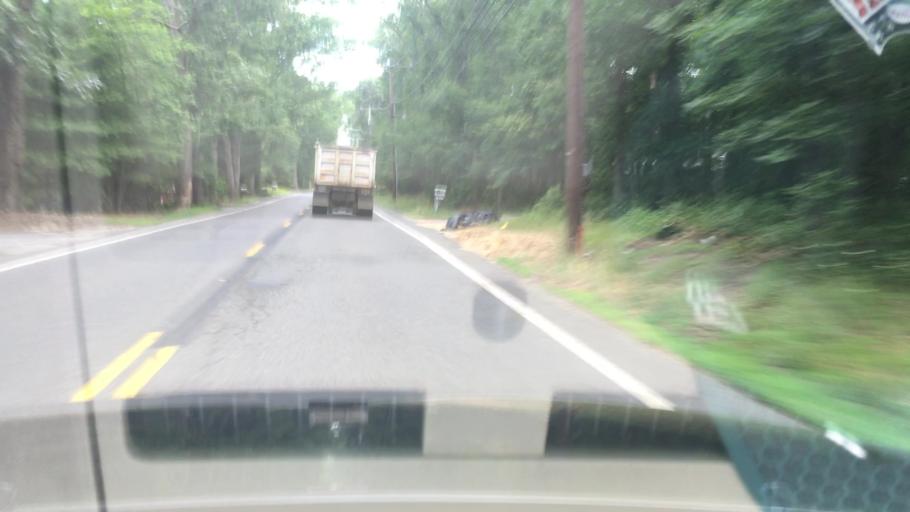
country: US
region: New Jersey
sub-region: Ocean County
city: Vista Center
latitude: 40.1156
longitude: -74.3912
